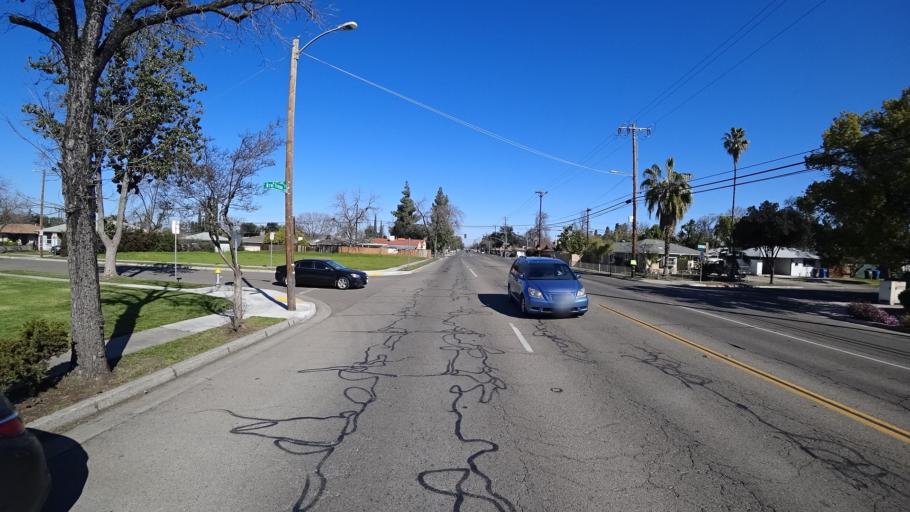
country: US
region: California
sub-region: Fresno County
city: Fresno
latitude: 36.7749
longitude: -119.7816
